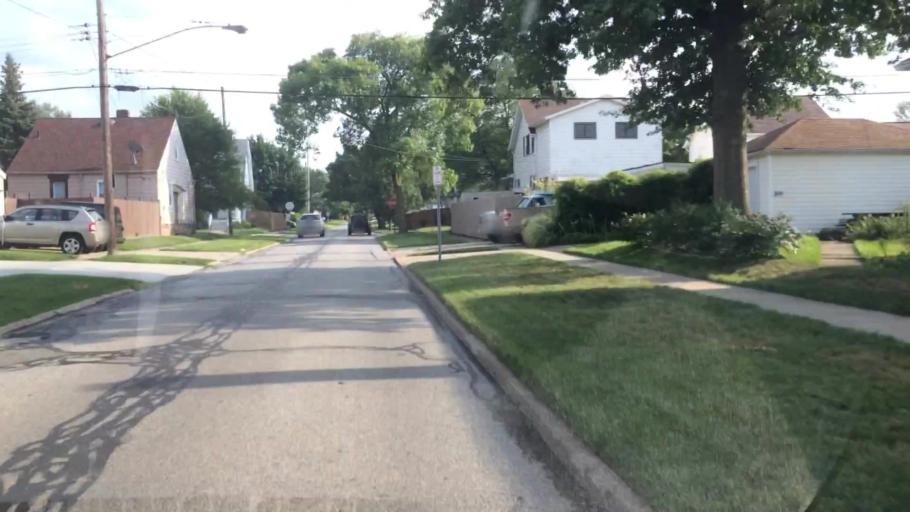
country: US
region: Ohio
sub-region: Cuyahoga County
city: Parma
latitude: 41.4153
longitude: -81.7384
